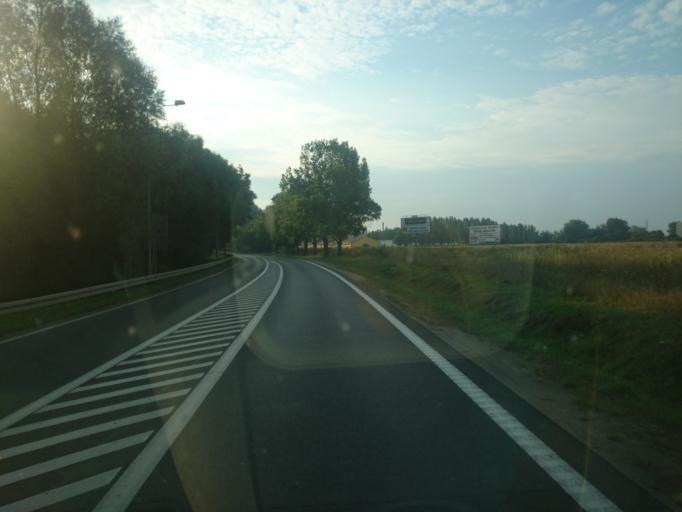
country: PL
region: Lubusz
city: Gorzow Wielkopolski
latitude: 52.7436
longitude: 15.1664
